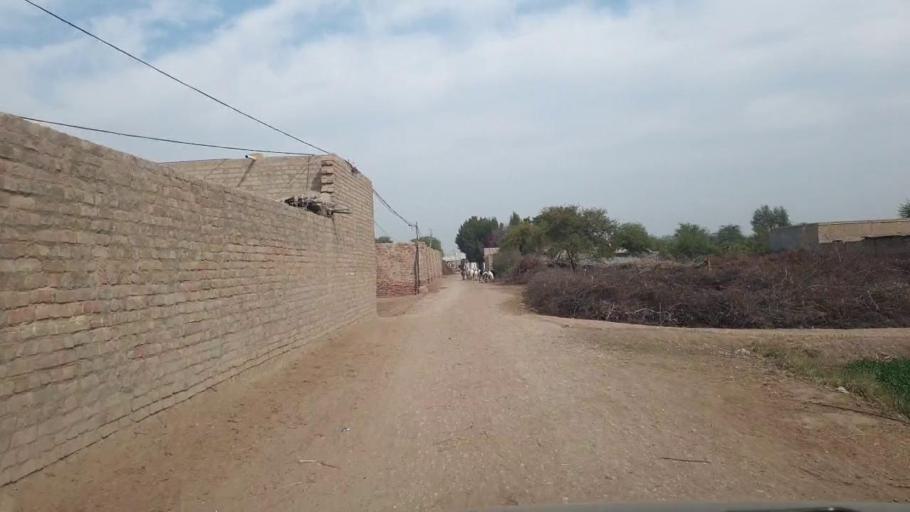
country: PK
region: Sindh
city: Shahdadpur
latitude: 25.9419
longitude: 68.6825
